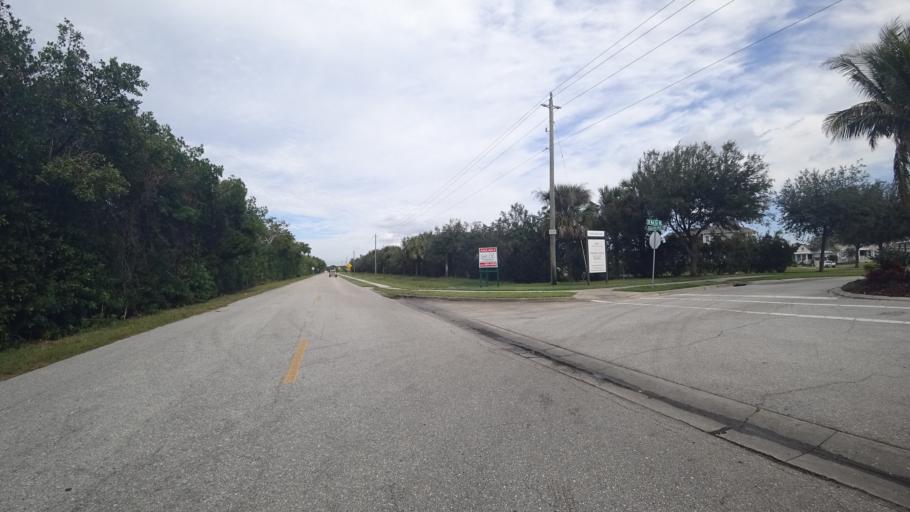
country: US
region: Florida
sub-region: Manatee County
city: Cortez
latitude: 27.4671
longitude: -82.6452
